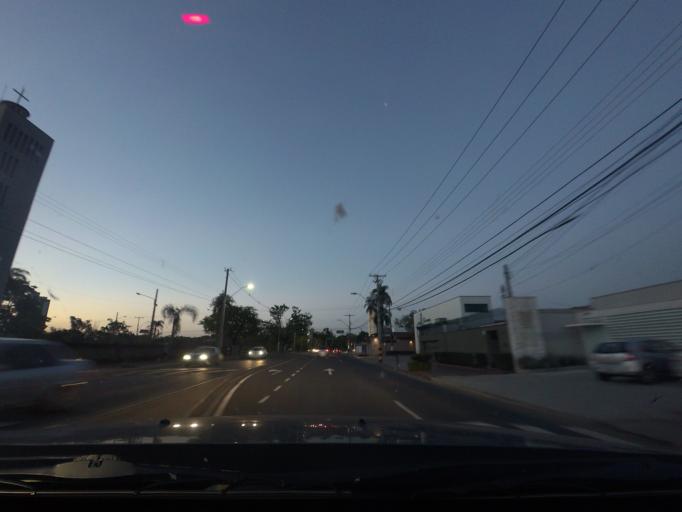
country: BR
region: Sao Paulo
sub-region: Piracicaba
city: Piracicaba
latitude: -22.7166
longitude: -47.6328
